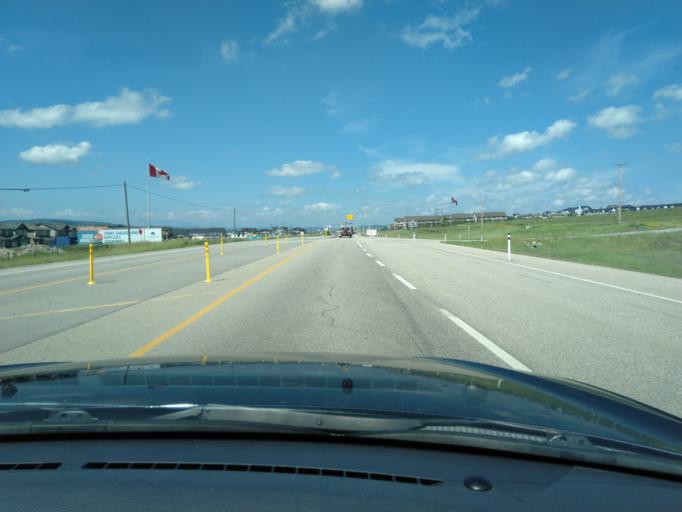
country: CA
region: Alberta
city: Cochrane
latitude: 51.2025
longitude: -114.4997
